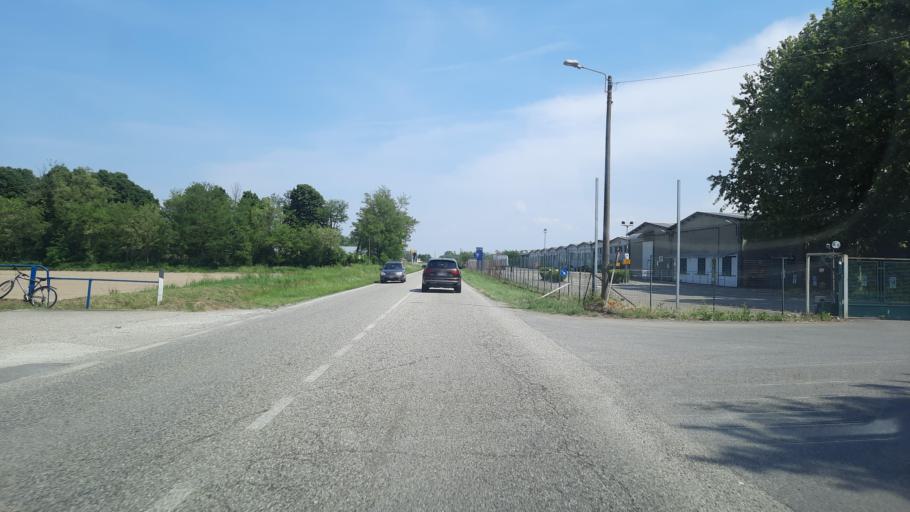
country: IT
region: Lombardy
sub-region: Provincia di Pavia
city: Villanova d'Ardenghi
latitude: 45.1647
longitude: 9.0188
